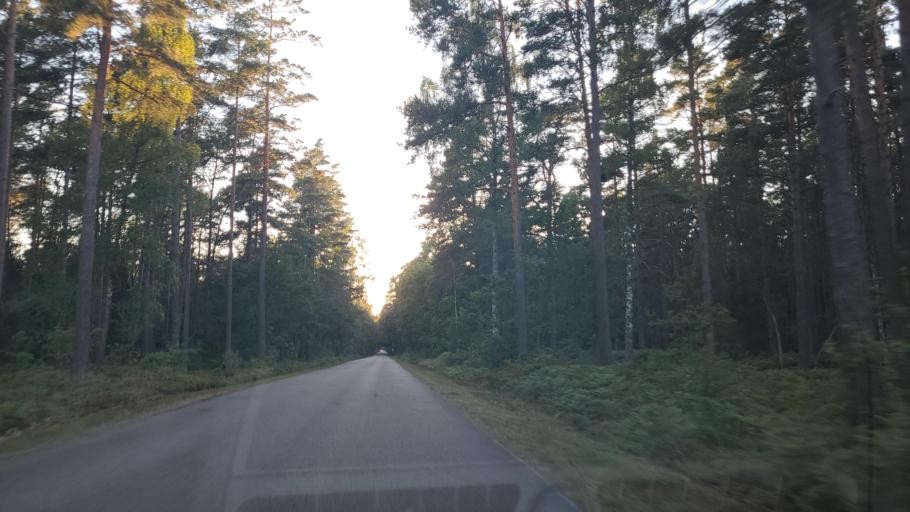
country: SE
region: Kalmar
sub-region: Borgholms Kommun
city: Borgholm
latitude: 57.2765
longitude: 17.0375
